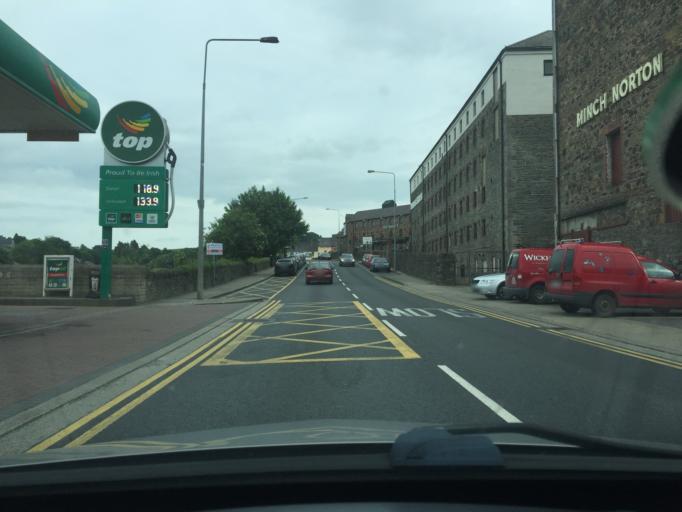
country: IE
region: Leinster
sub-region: Loch Garman
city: Enniscorthy
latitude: 52.5036
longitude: -6.5689
